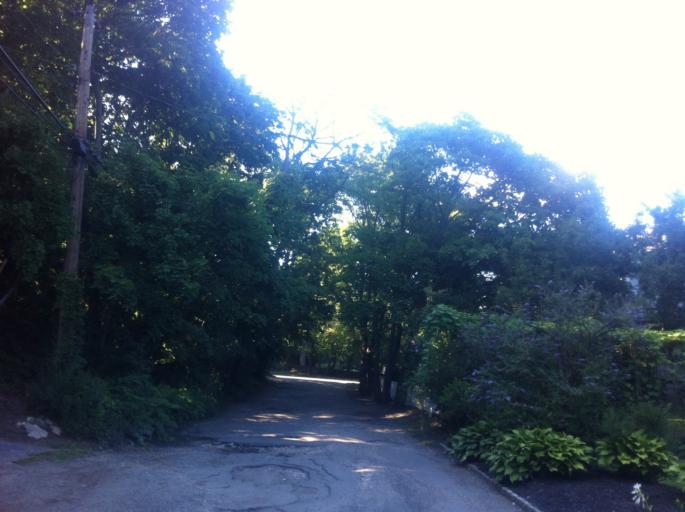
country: US
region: New York
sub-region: Nassau County
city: Bayville
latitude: 40.9084
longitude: -73.5578
